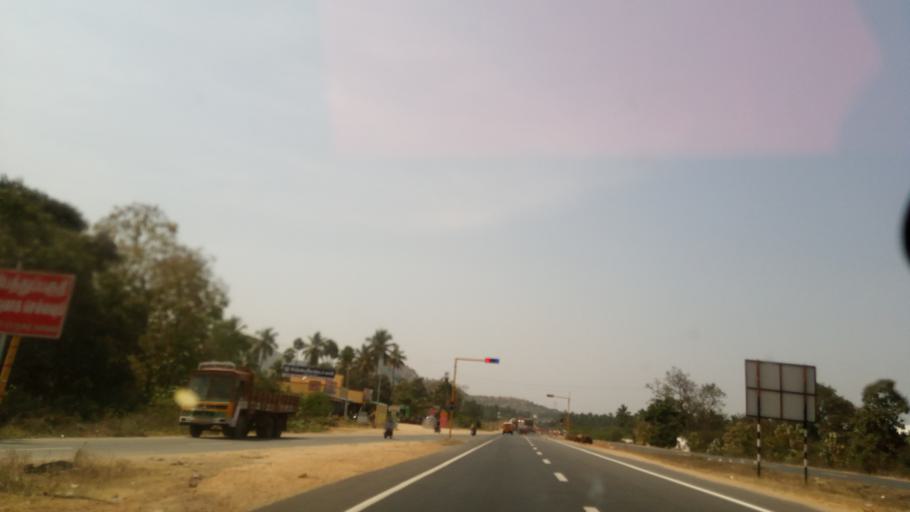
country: IN
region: Tamil Nadu
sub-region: Salem
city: Salem
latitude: 11.6613
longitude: 78.2255
